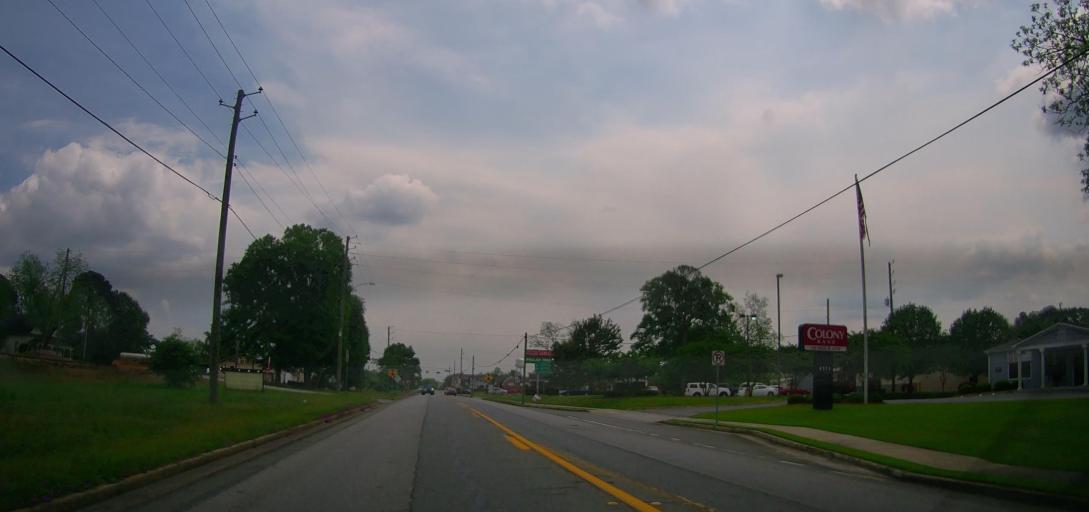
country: US
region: Georgia
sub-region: Treutlen County
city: Soperton
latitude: 32.3801
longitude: -82.5956
